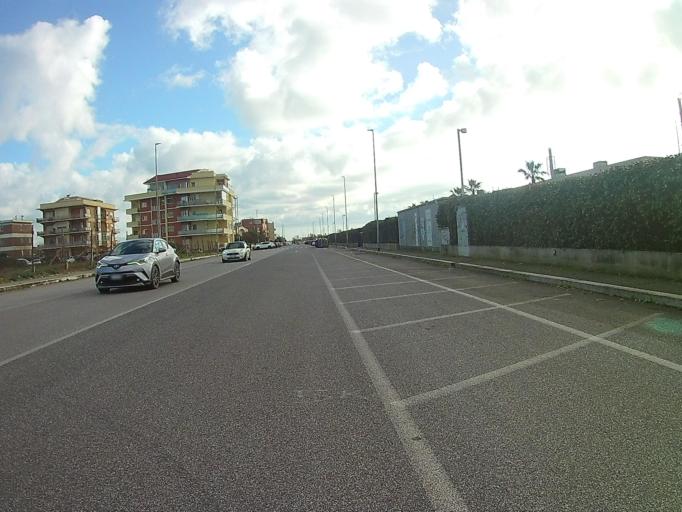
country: IT
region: Latium
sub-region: Citta metropolitana di Roma Capitale
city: Lido di Ostia
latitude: 41.7223
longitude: 12.2985
